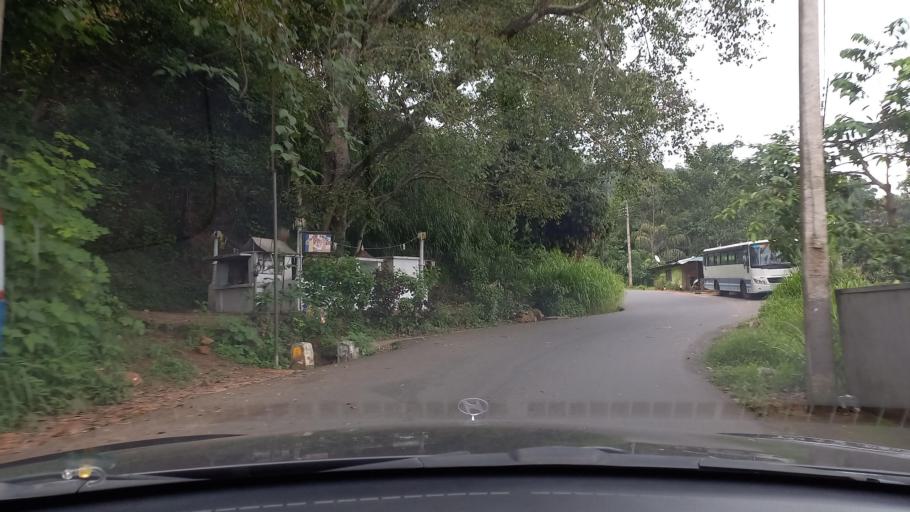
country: LK
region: Central
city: Kandy
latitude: 7.2328
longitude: 80.6041
